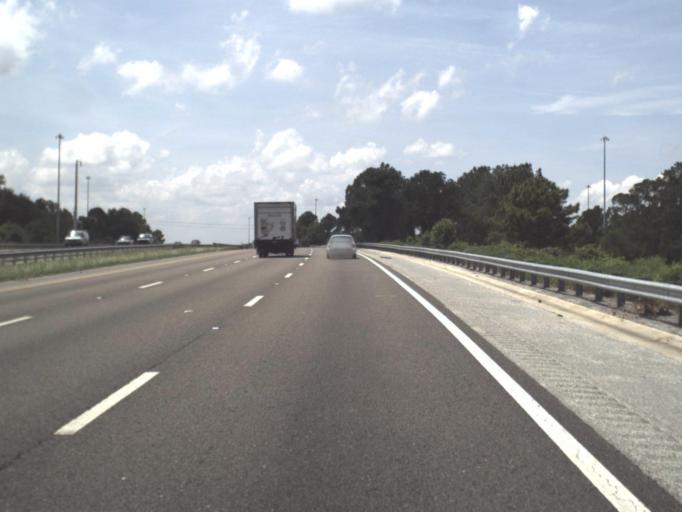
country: US
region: Florida
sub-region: Saint Johns County
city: Fruit Cove
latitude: 30.1805
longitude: -81.6261
